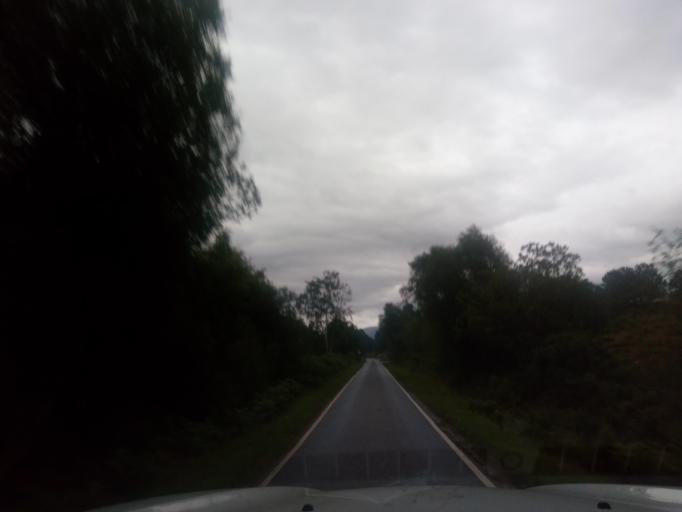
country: GB
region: Scotland
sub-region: Highland
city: Fort William
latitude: 56.8472
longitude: -5.3009
